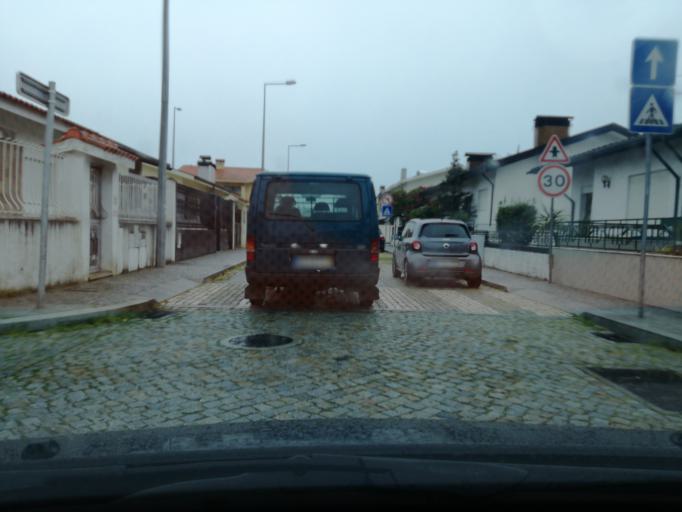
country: PT
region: Porto
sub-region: Maia
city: Gemunde
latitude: 41.2569
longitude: -8.6642
